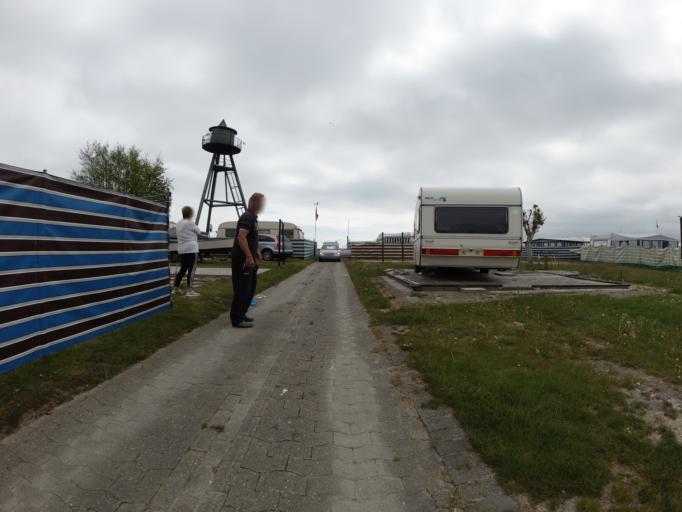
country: DE
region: Lower Saxony
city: Schillig
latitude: 53.6966
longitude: 8.0275
